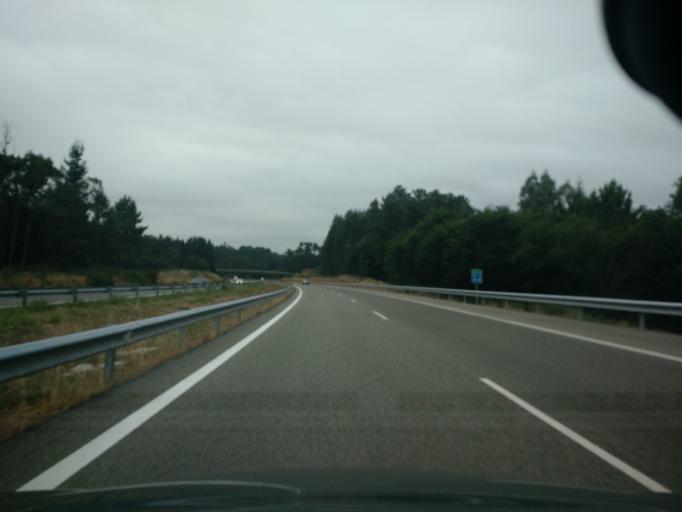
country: ES
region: Galicia
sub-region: Provincia da Coruna
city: Ordes
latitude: 43.0617
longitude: -8.3698
